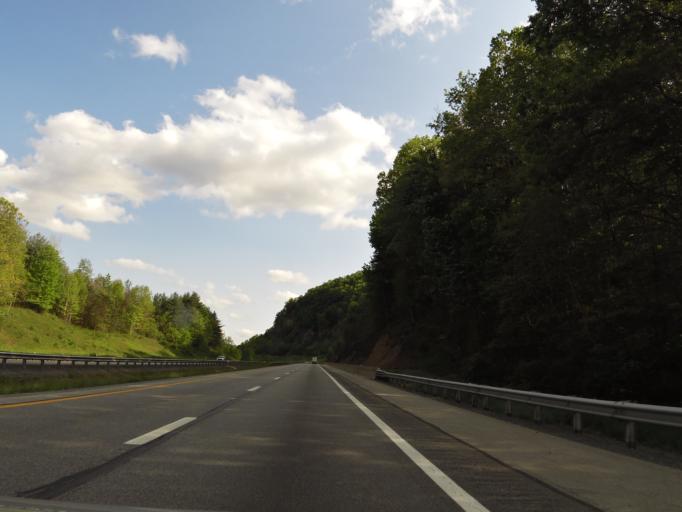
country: US
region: West Virginia
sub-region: Mercer County
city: Athens
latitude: 37.4671
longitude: -81.0672
